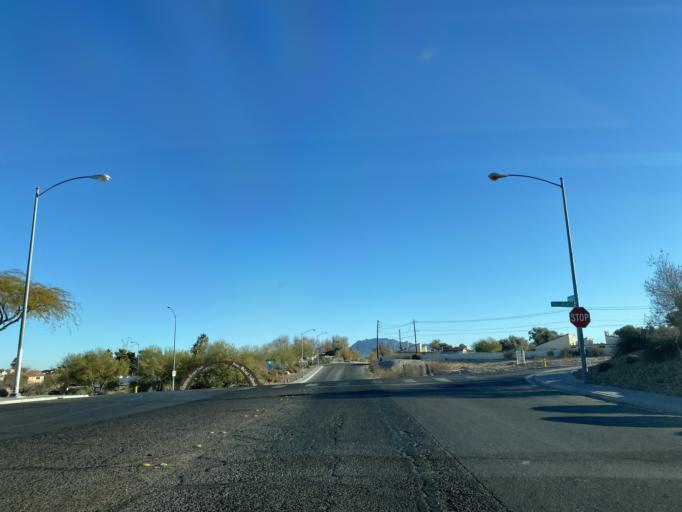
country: US
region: Nevada
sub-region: Clark County
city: Winchester
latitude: 36.1250
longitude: -115.1091
